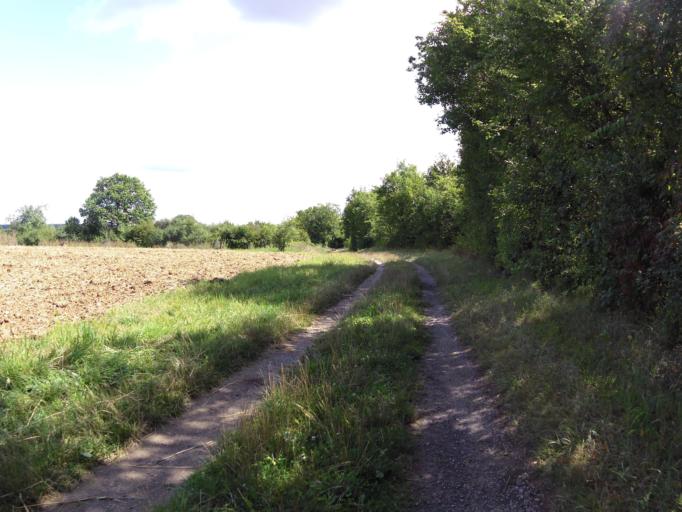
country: DE
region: Bavaria
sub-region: Regierungsbezirk Unterfranken
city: Margetshochheim
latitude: 49.8292
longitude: 9.8559
